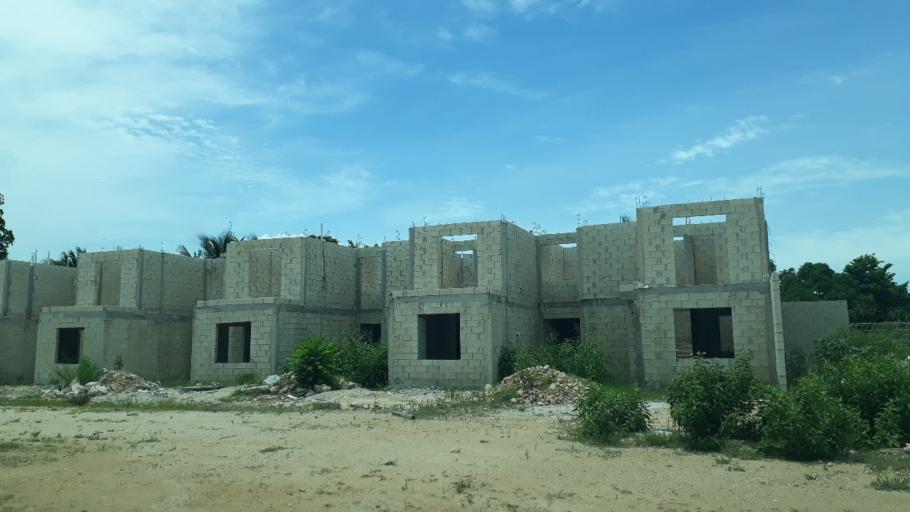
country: MX
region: Quintana Roo
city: Calderitas
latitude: 18.5588
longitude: -88.2565
